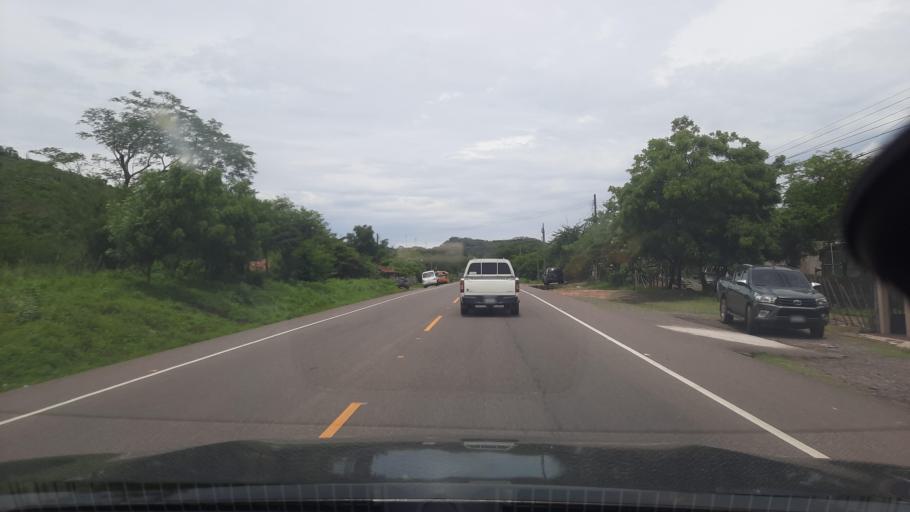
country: HN
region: Valle
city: Langue
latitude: 13.5861
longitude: -87.6915
